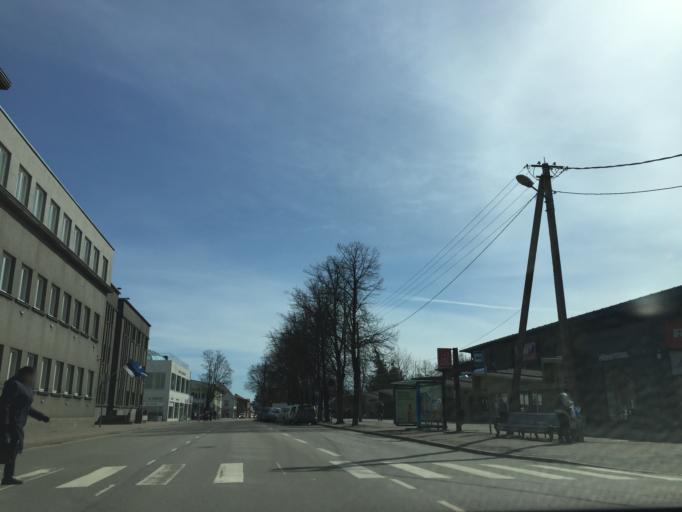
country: EE
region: Paernumaa
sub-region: Paernu linn
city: Parnu
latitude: 58.3825
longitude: 24.5093
